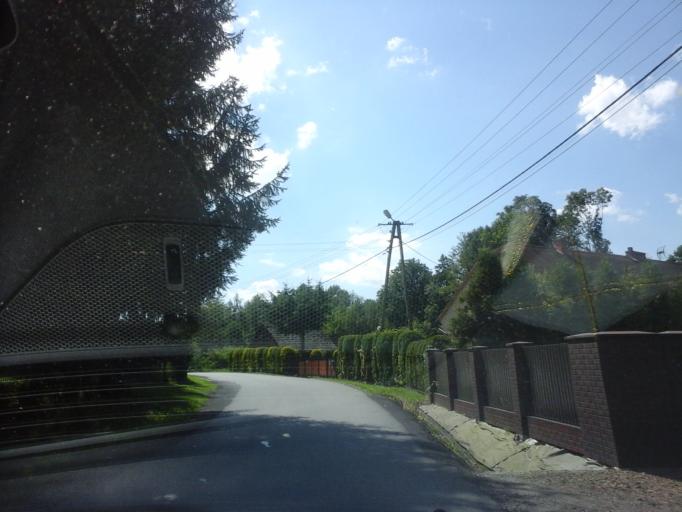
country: PL
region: Lesser Poland Voivodeship
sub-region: Powiat wadowicki
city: Spytkowice
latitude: 49.9905
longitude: 19.5044
